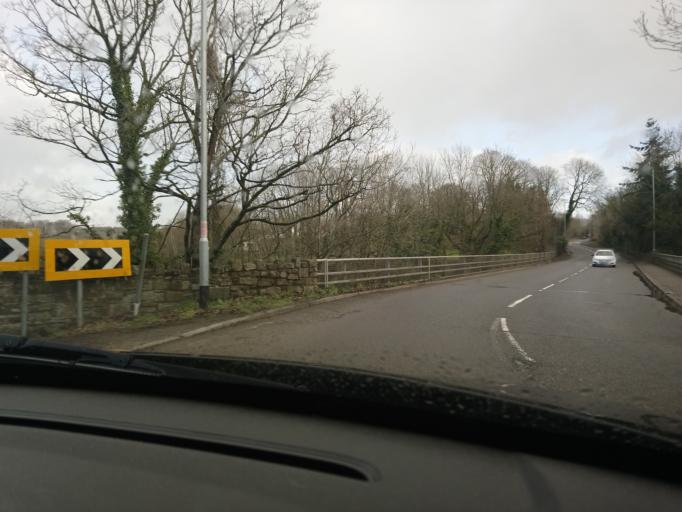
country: GB
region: Wales
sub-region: Wrexham
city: Ruabon
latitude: 52.9687
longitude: -3.0626
